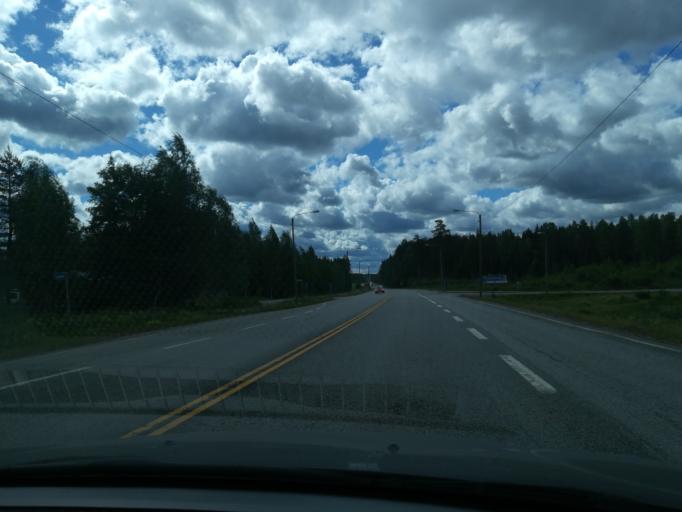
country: FI
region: Southern Savonia
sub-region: Mikkeli
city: Ristiina
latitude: 61.5009
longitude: 27.2383
